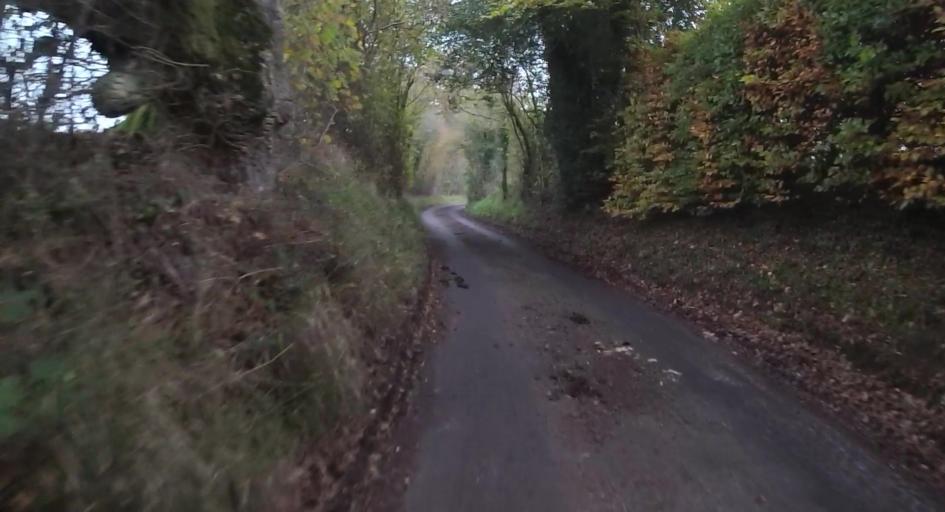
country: GB
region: England
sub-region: Surrey
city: Farnham
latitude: 51.1695
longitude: -0.8148
